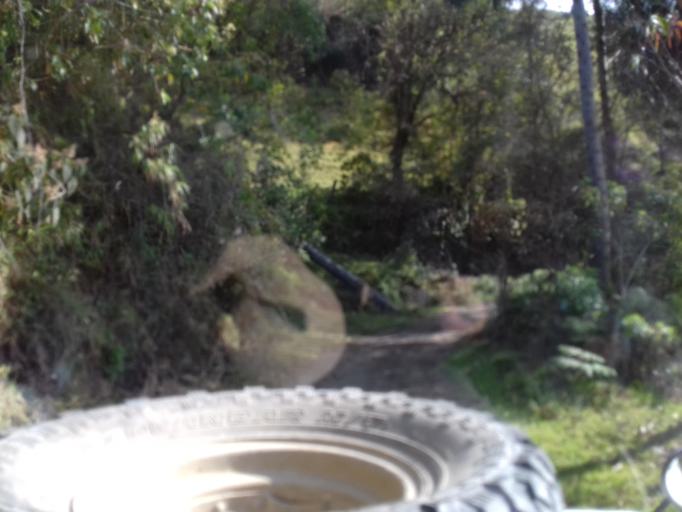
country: CO
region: Tolima
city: Cajamarca
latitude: 4.5334
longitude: -75.4304
